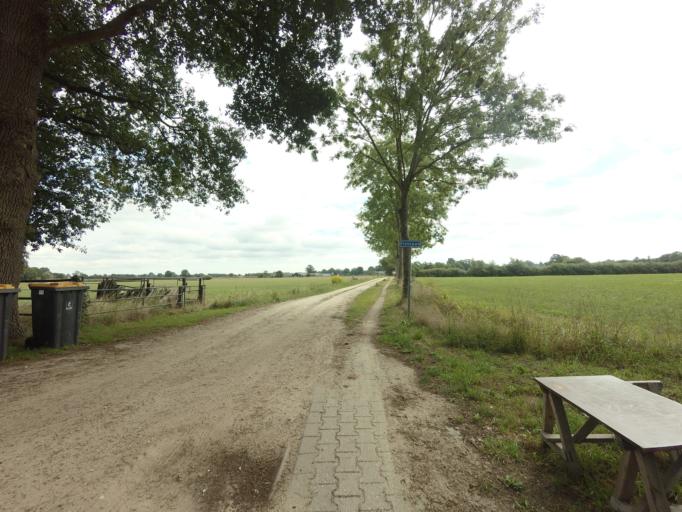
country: NL
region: Gelderland
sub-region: Gemeente Lochem
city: Harfsen
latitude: 52.2790
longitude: 6.3286
